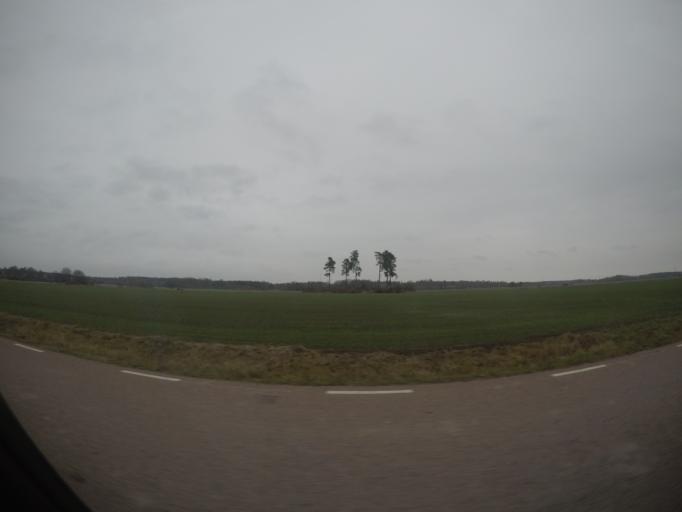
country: SE
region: Vaestmanland
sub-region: Kopings Kommun
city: Koping
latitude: 59.5633
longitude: 16.0943
